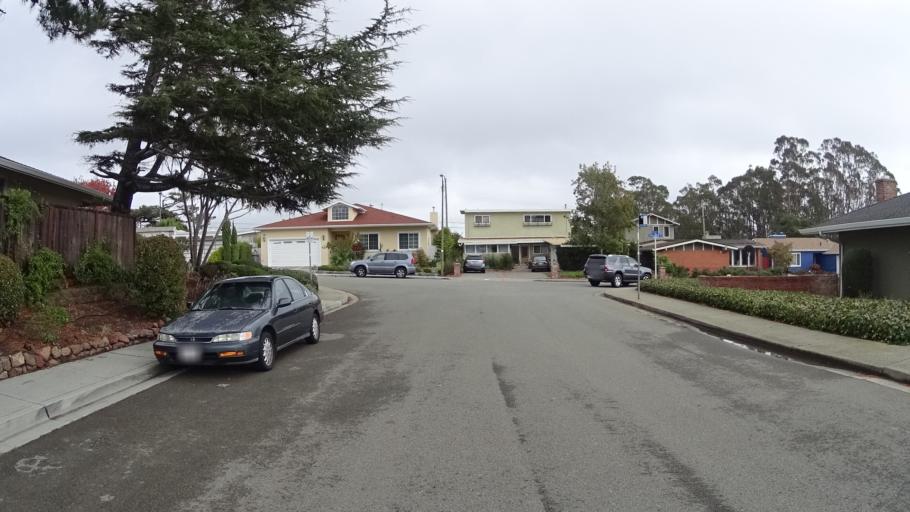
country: US
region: California
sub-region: San Mateo County
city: San Bruno
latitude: 37.6043
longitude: -122.4162
